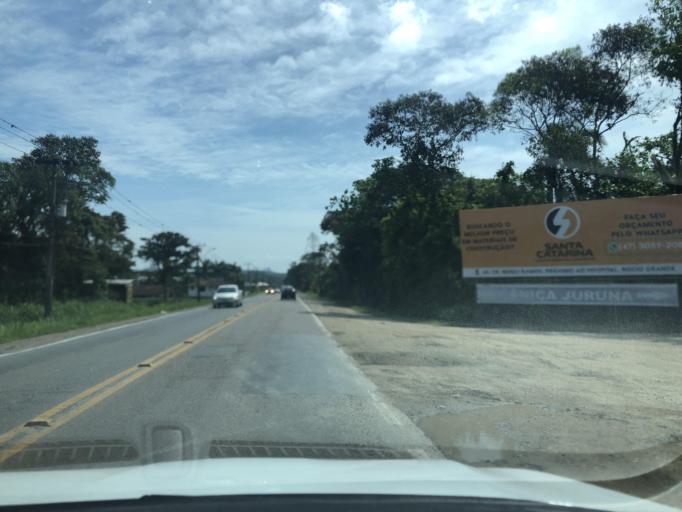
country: BR
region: Santa Catarina
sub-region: Sao Francisco Do Sul
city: Sao Francisco do Sul
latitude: -26.2460
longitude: -48.6033
